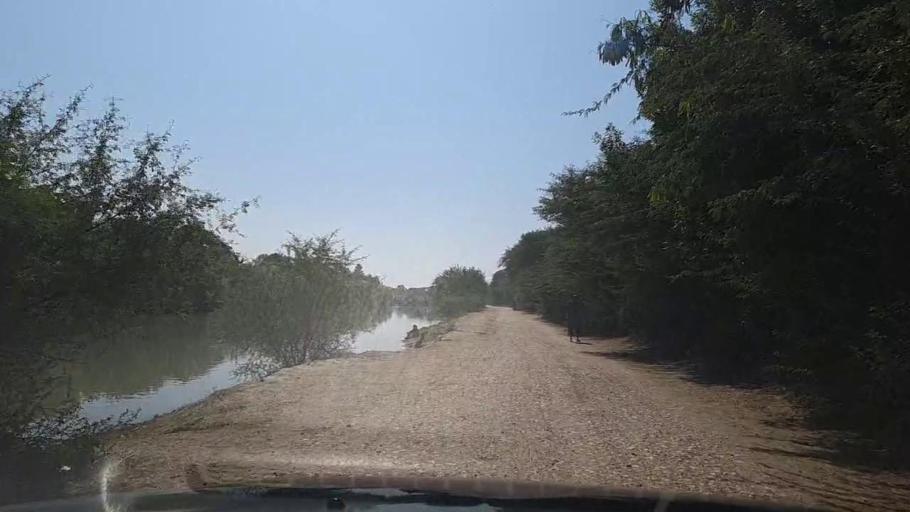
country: PK
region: Sindh
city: Thatta
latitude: 24.5993
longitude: 67.8202
